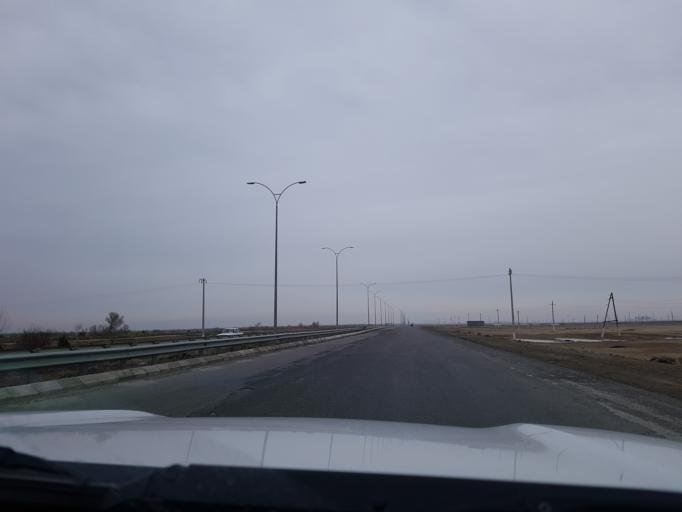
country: TM
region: Ahal
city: Tejen
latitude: 37.3560
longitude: 60.4305
